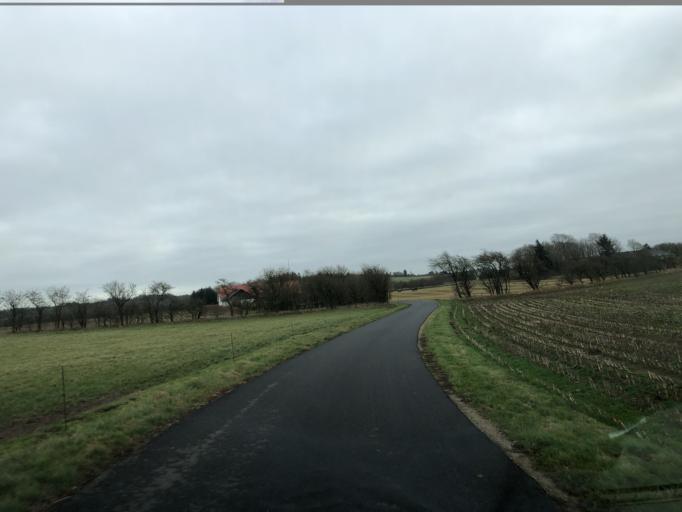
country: DK
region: Central Jutland
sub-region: Viborg Kommune
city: Stoholm
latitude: 56.4504
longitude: 9.1215
